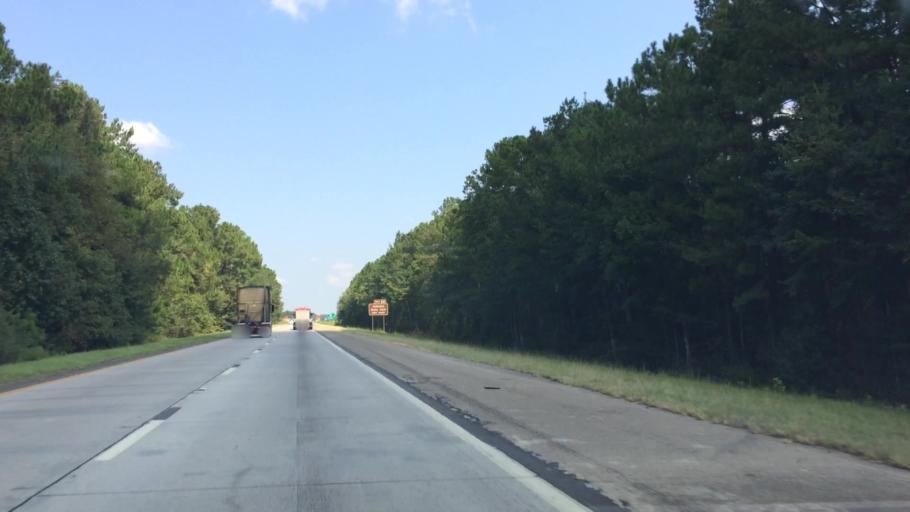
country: US
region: South Carolina
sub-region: Dorchester County
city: Saint George
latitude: 33.0742
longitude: -80.6573
